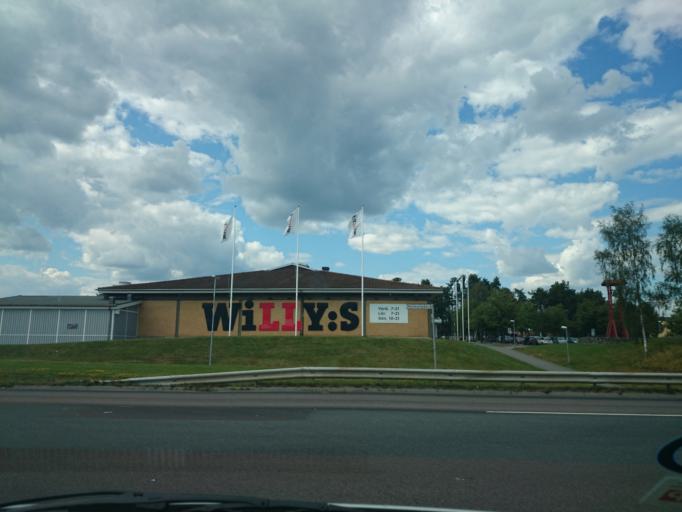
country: SE
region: Joenkoeping
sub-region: Varnamo Kommun
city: Varnamo
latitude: 57.1831
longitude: 14.0270
